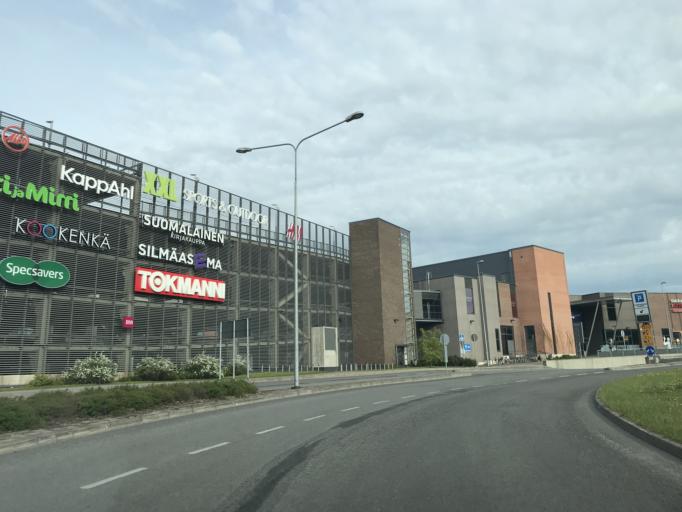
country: FI
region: Varsinais-Suomi
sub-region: Turku
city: Turku
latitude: 60.4307
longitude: 22.3187
